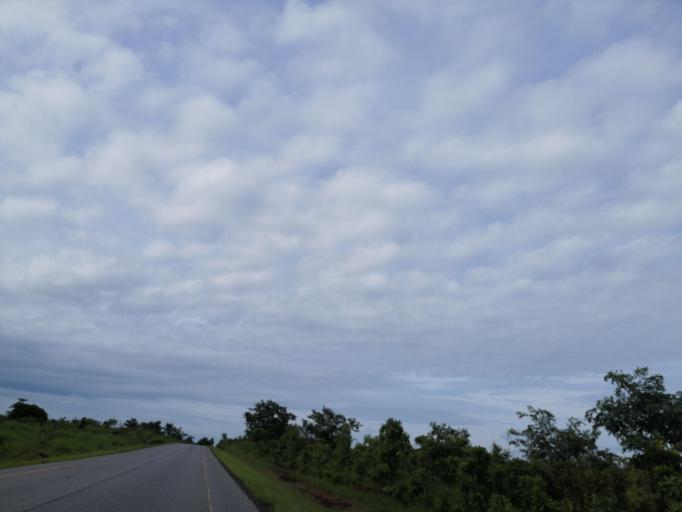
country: SL
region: Northern Province
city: Port Loko
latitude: 8.7784
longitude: -12.8572
